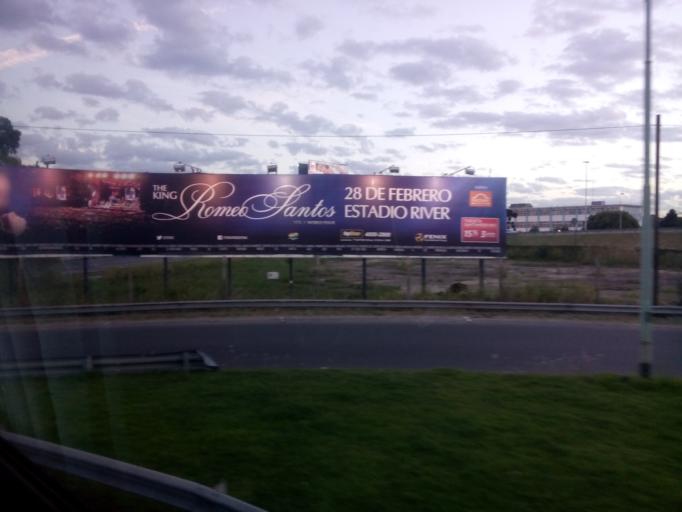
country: AR
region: Buenos Aires F.D.
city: Retiro
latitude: -34.5709
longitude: -58.3993
